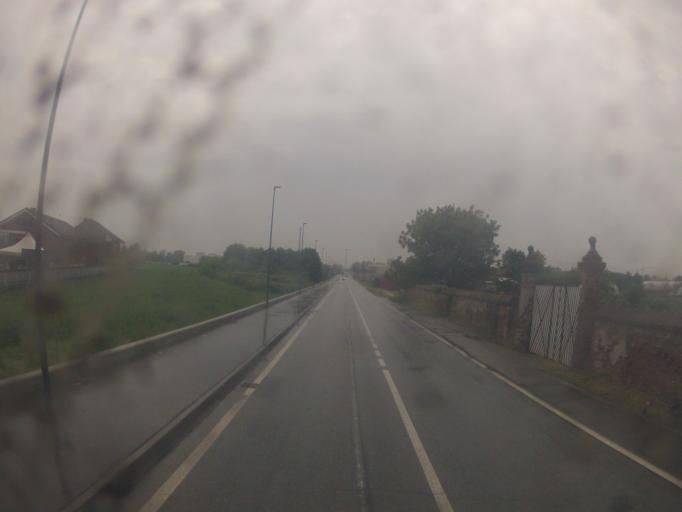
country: IT
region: Piedmont
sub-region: Provincia di Torino
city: La Loggia
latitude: 44.9437
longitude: 7.6700
